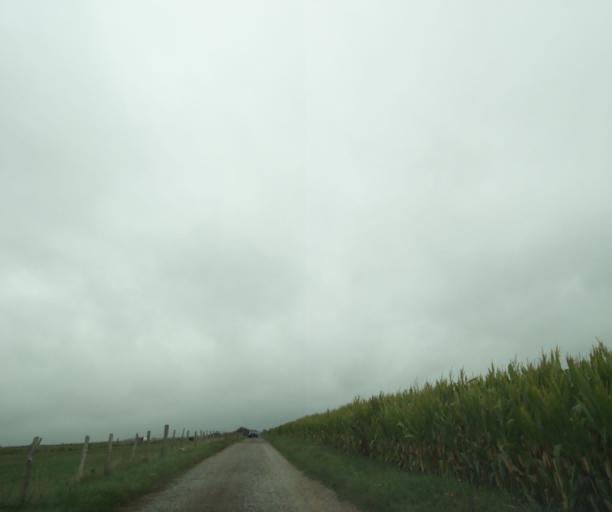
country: FR
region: Nord-Pas-de-Calais
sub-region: Departement du Pas-de-Calais
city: Etaples
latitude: 50.5211
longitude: 1.6831
